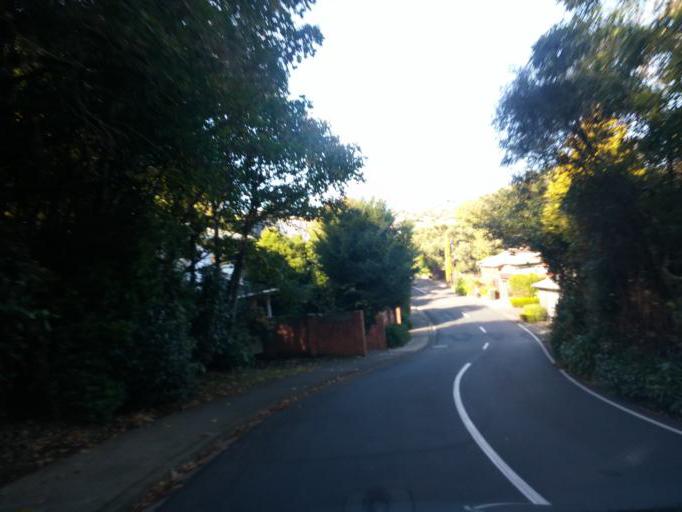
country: NZ
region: Wellington
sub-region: Wellington City
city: Kelburn
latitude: -41.2458
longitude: 174.7828
